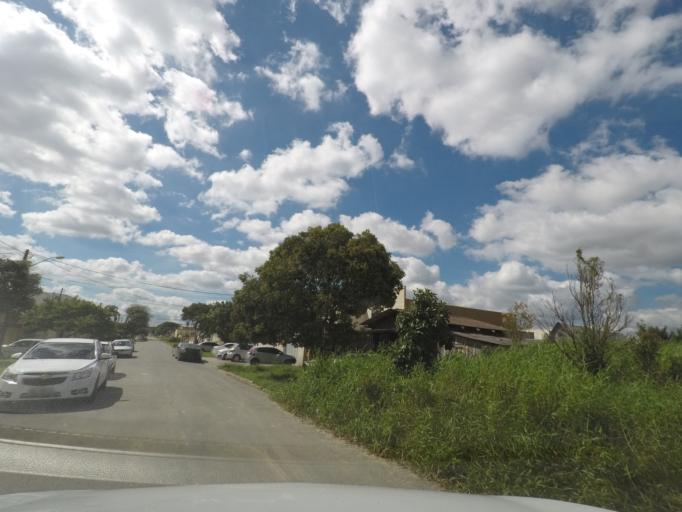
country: BR
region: Parana
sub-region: Sao Jose Dos Pinhais
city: Sao Jose dos Pinhais
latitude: -25.5053
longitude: -49.2166
